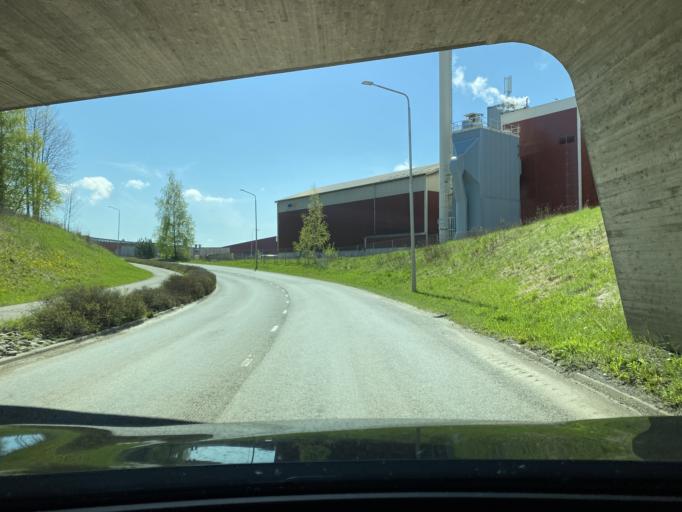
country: FI
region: Pirkanmaa
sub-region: Lounais-Pirkanmaa
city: Vammala
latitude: 61.3494
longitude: 22.8825
